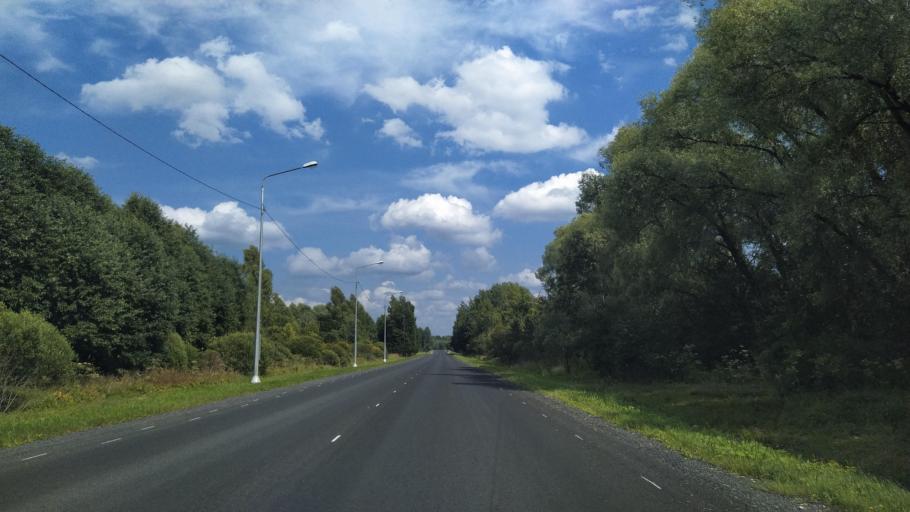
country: RU
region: Pskov
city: Porkhov
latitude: 57.7256
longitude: 29.2784
